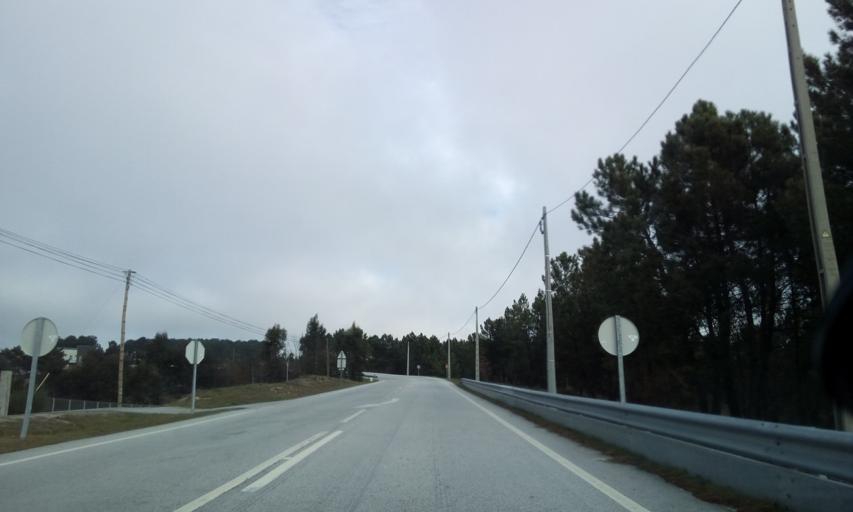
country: PT
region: Guarda
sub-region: Aguiar da Beira
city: Aguiar da Beira
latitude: 40.7854
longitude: -7.5023
